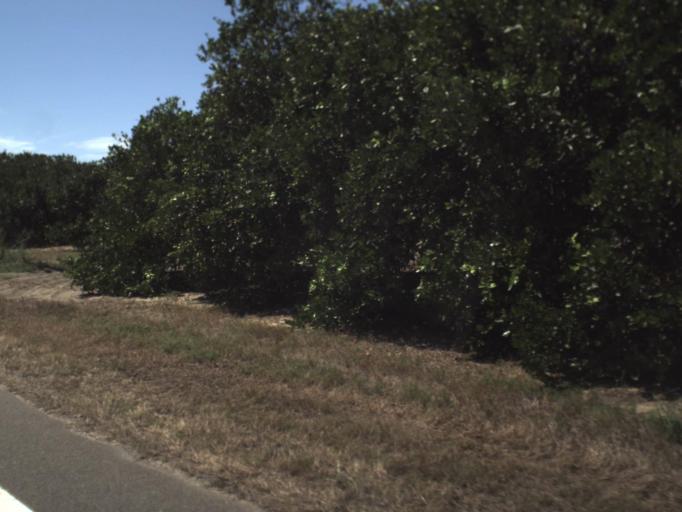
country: US
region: Florida
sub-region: Polk County
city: Babson Park
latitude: 27.8180
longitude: -81.5311
